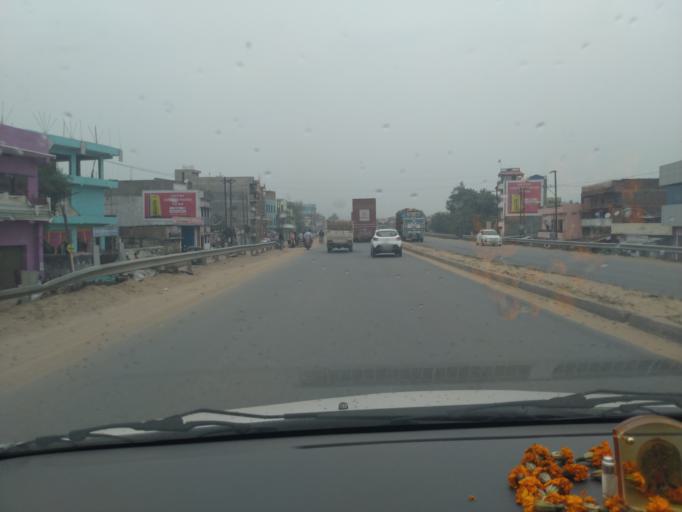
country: IN
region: Bihar
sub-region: Rohtas
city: Dehri
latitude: 24.9082
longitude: 84.1839
